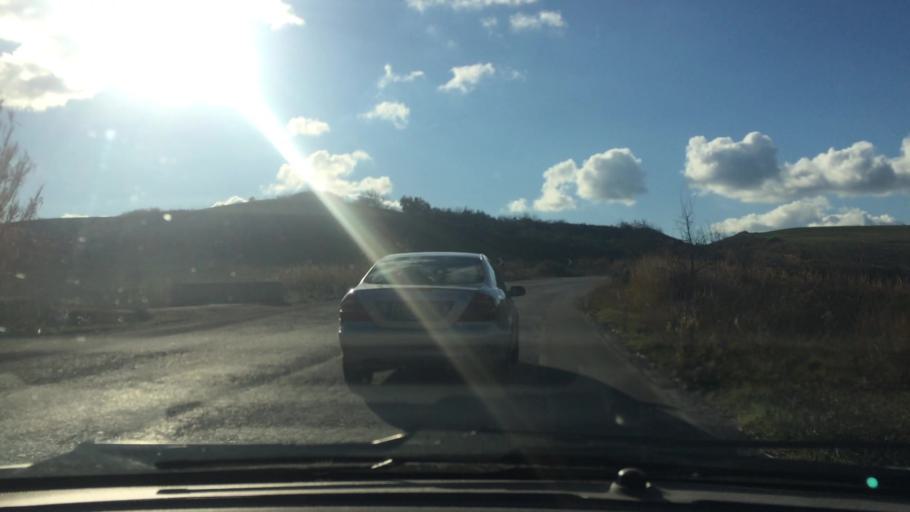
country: IT
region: Basilicate
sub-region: Provincia di Potenza
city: Tolve
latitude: 40.7185
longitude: 16.0346
